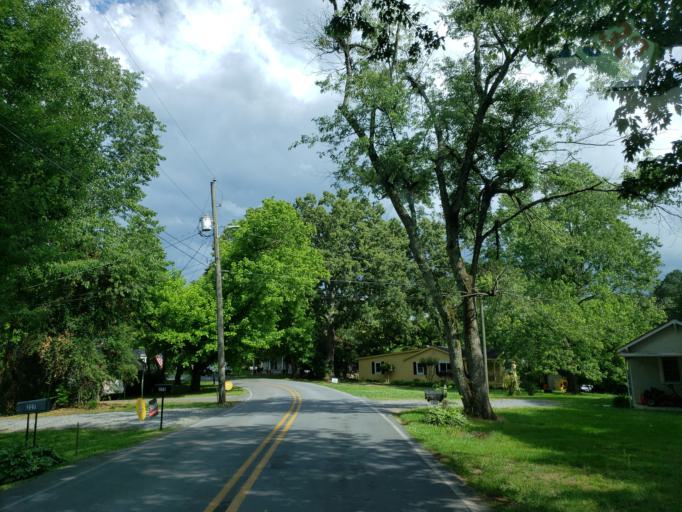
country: US
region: Georgia
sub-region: Pickens County
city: Jasper
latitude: 34.4633
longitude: -84.4251
